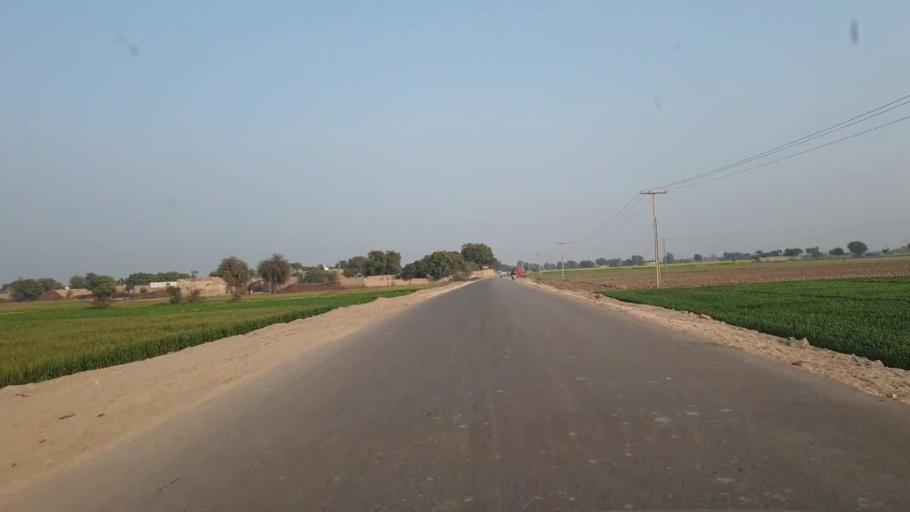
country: PK
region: Sindh
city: Hala
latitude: 25.8099
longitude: 68.4533
